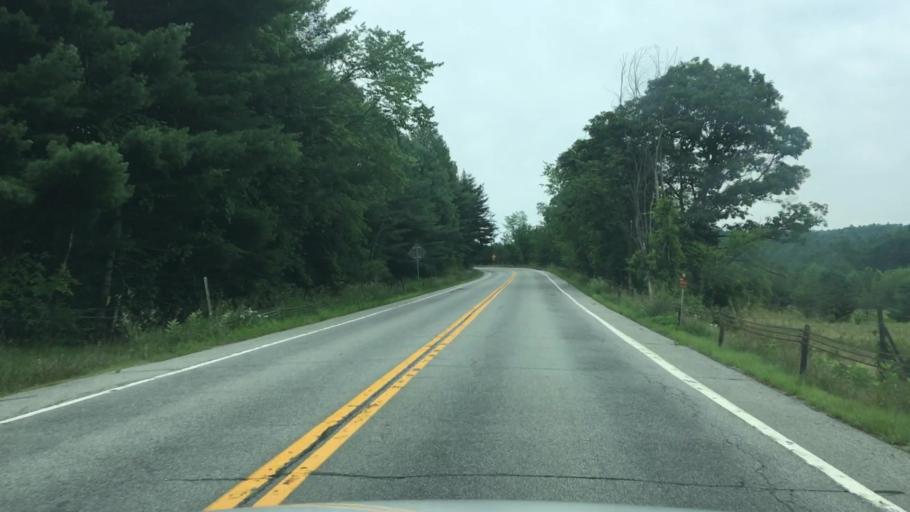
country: US
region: New York
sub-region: Essex County
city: Elizabethtown
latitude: 44.3863
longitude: -73.7125
